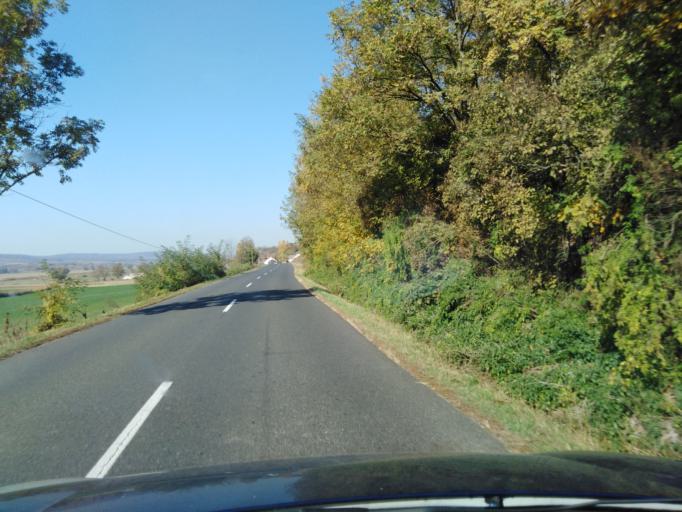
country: HU
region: Nograd
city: Karancskeszi
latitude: 48.1719
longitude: 19.6868
